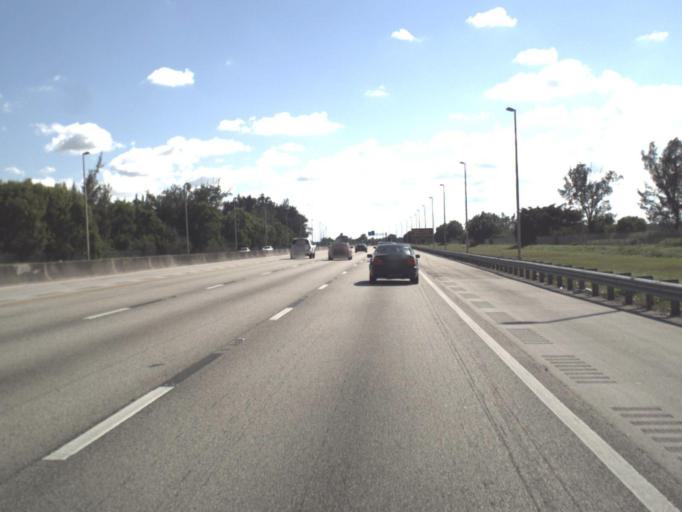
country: US
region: Florida
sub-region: Palm Beach County
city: Villages of Oriole
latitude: 26.4765
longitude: -80.1736
